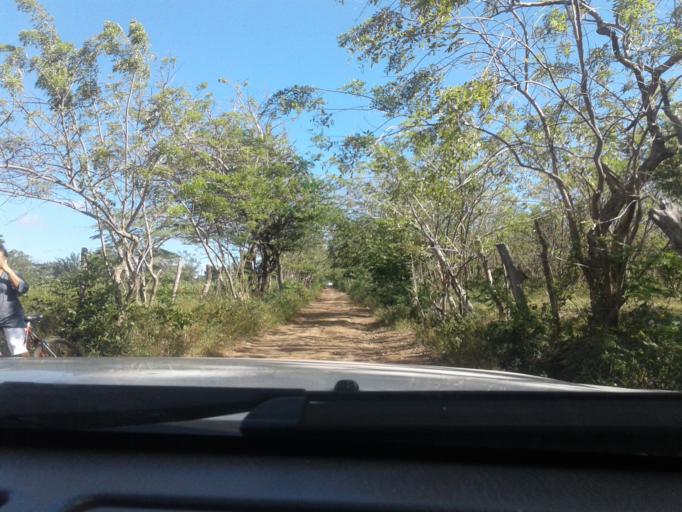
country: NI
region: Carazo
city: Santa Teresa
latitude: 11.7508
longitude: -86.1812
